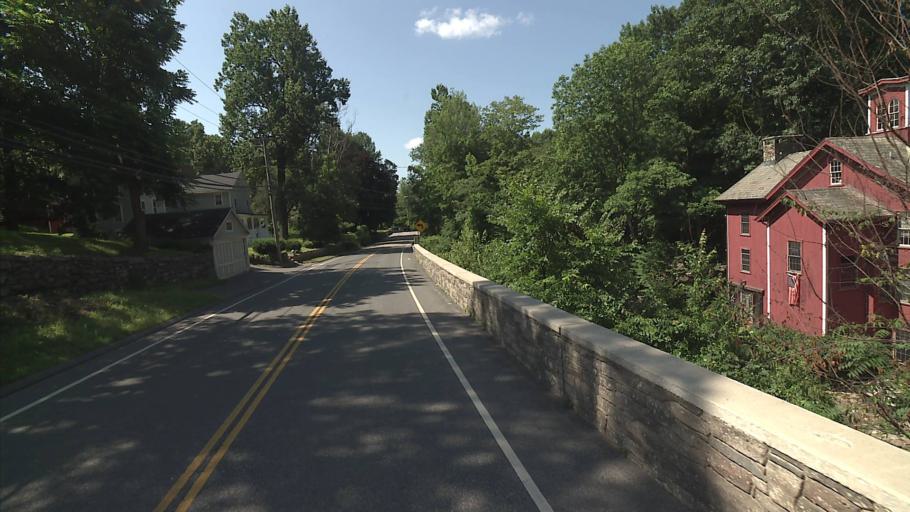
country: US
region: Connecticut
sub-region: Litchfield County
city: New Preston
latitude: 41.6798
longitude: -73.3546
